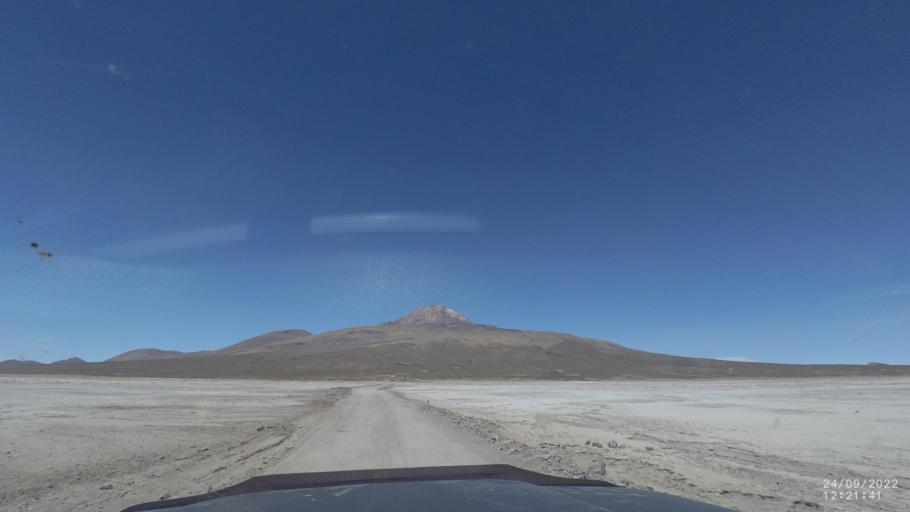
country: BO
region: Potosi
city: Colchani
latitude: -19.7504
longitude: -67.6679
